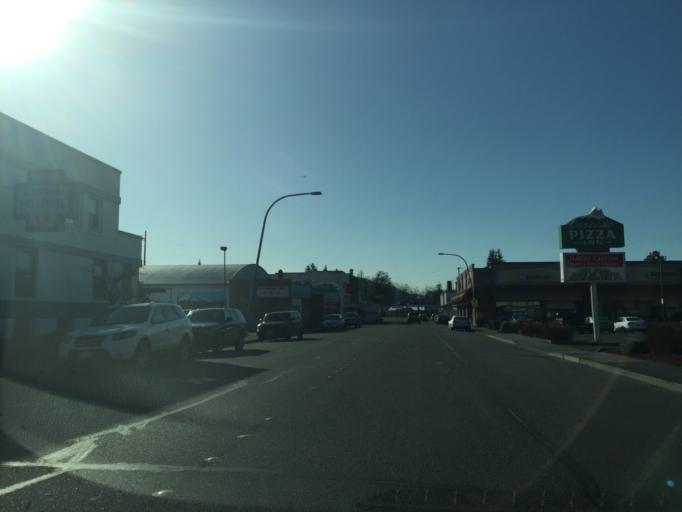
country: US
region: Washington
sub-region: Whatcom County
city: Bellingham
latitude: 48.7632
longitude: -122.4861
